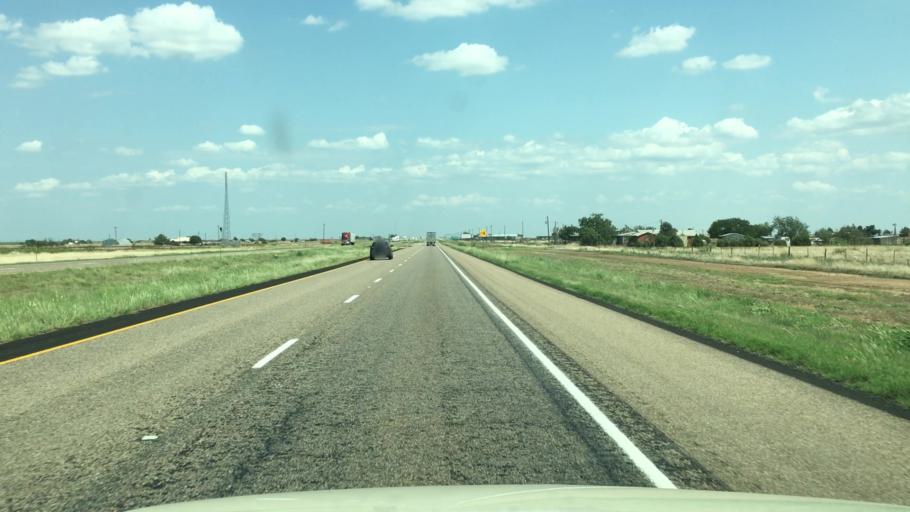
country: US
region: Texas
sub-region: Armstrong County
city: Claude
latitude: 35.0342
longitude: -101.1917
